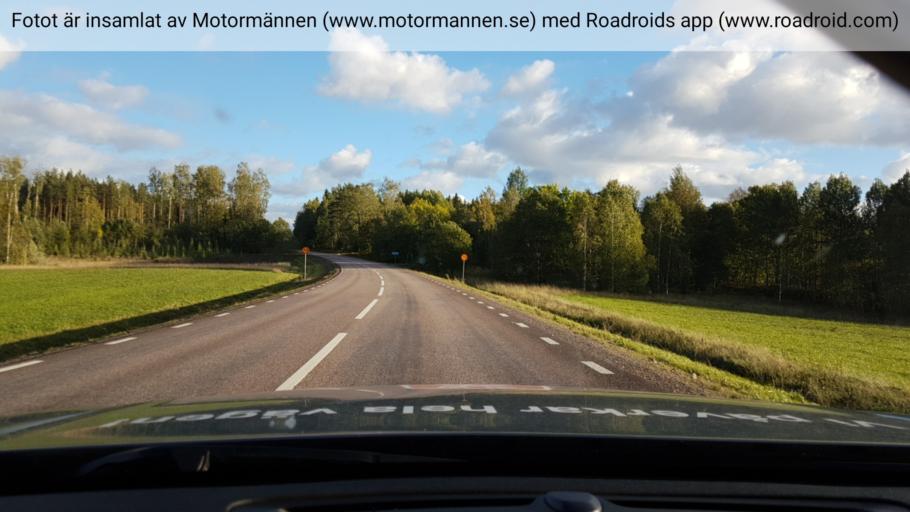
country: SE
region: Vaermland
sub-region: Karlstads Kommun
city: Molkom
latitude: 59.6155
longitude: 13.7299
